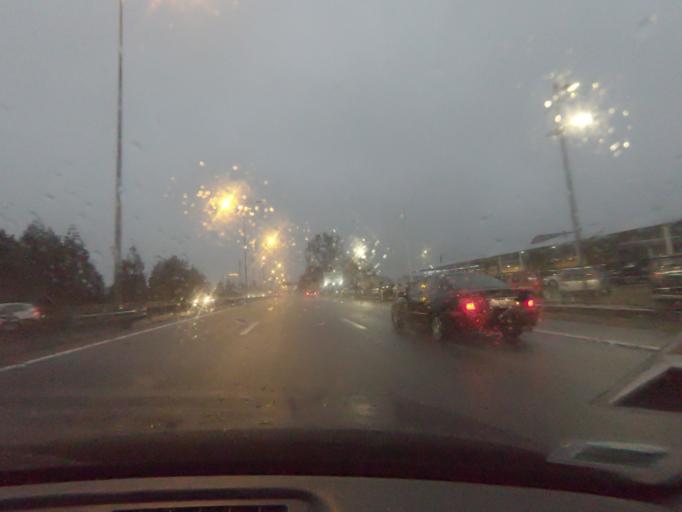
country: PT
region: Porto
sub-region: Matosinhos
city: Santa Cruz do Bispo
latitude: 41.2139
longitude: -8.6904
